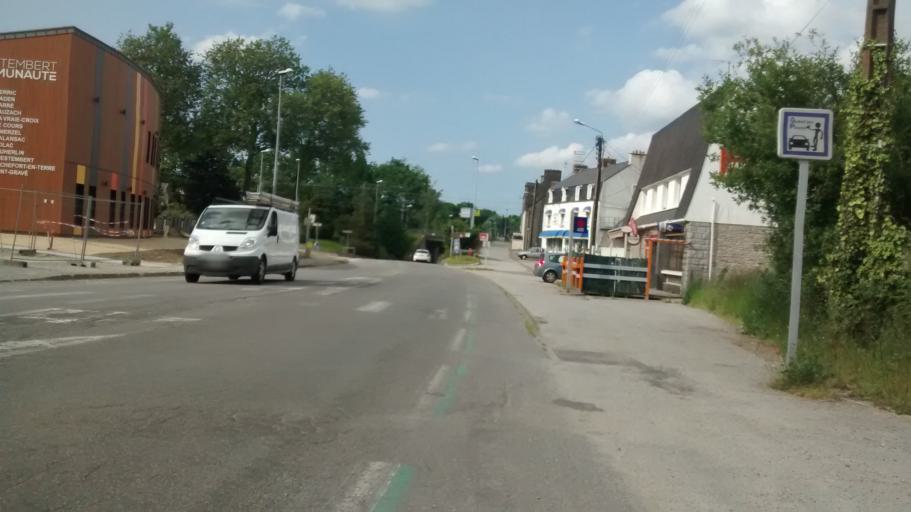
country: FR
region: Brittany
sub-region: Departement du Morbihan
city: Questembert
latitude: 47.6817
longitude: -2.4490
